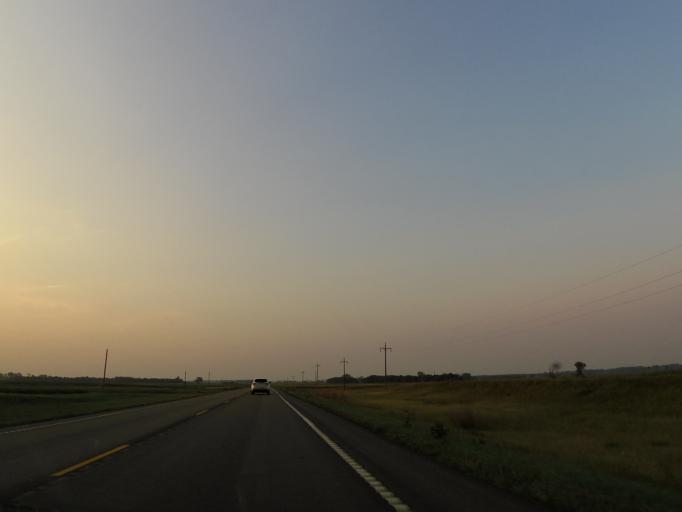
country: US
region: North Dakota
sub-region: Grand Forks County
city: Larimore
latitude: 48.1055
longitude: -97.6224
